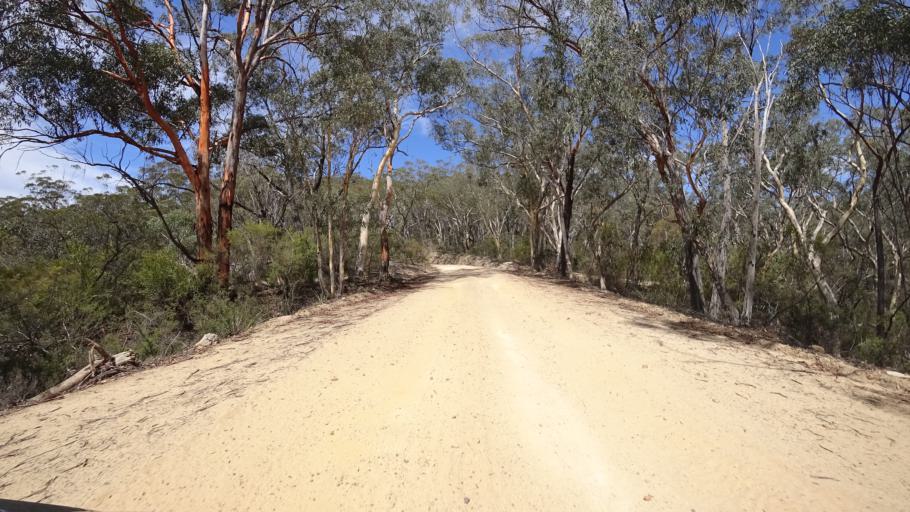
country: AU
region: New South Wales
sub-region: Lithgow
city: Lithgow
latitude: -33.2600
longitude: 150.2208
